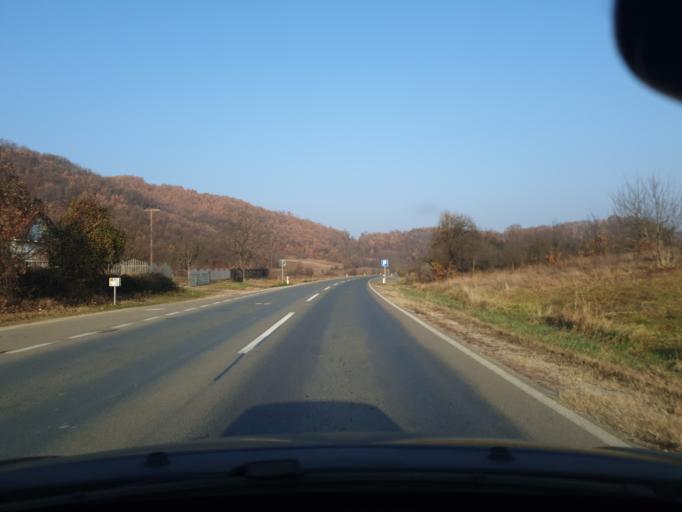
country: RS
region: Central Serbia
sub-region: Jablanicki Okrug
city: Vlasotince
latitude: 42.8978
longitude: 22.0469
